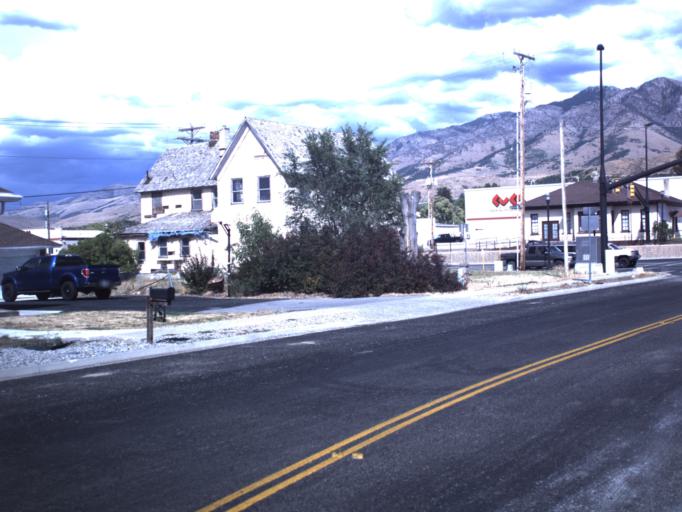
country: US
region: Utah
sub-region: Cache County
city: Richmond
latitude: 41.9227
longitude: -111.8152
